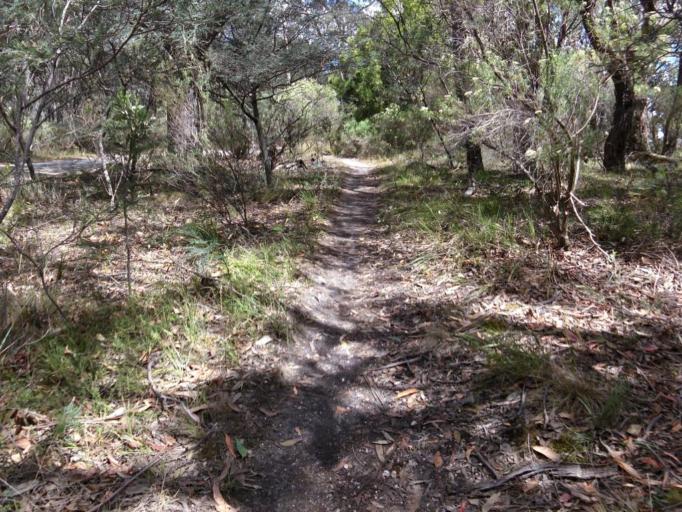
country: AU
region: Victoria
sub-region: Melton
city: Melton West
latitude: -37.4922
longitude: 144.5483
